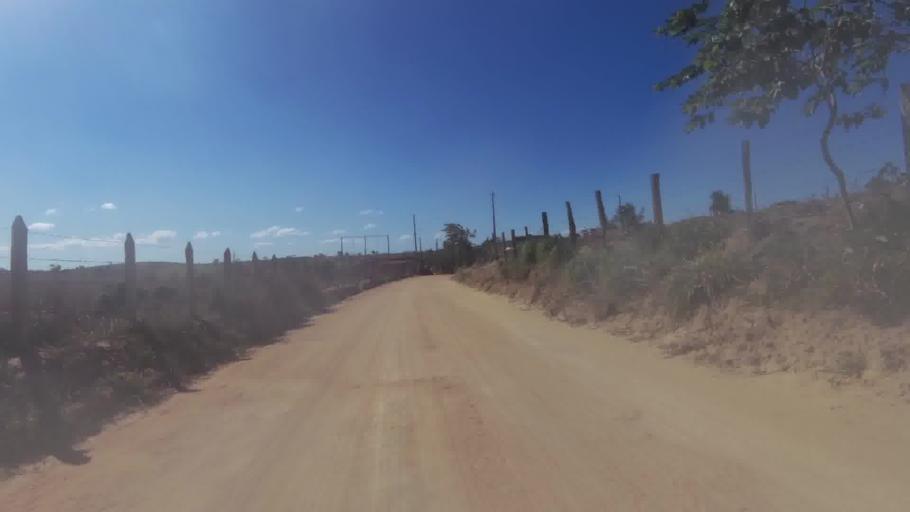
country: BR
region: Espirito Santo
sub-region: Marataizes
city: Marataizes
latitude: -21.1521
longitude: -40.9829
